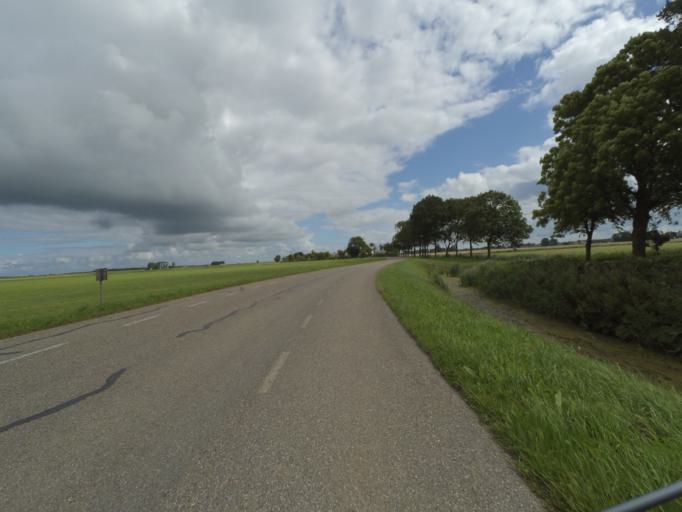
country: NL
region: Groningen
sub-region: Gemeente Zuidhorn
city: Grijpskerk
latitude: 53.3013
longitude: 6.2496
